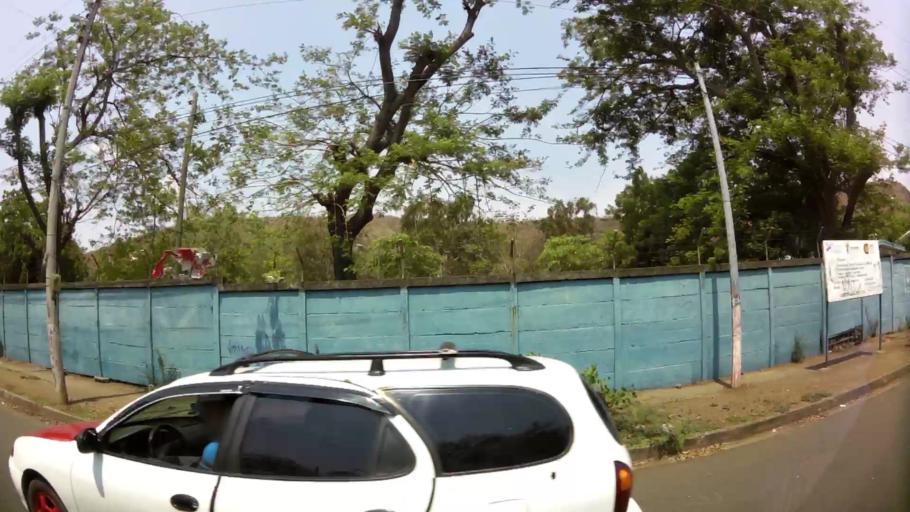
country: NI
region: Managua
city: Ciudad Sandino
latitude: 12.1555
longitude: -86.3148
